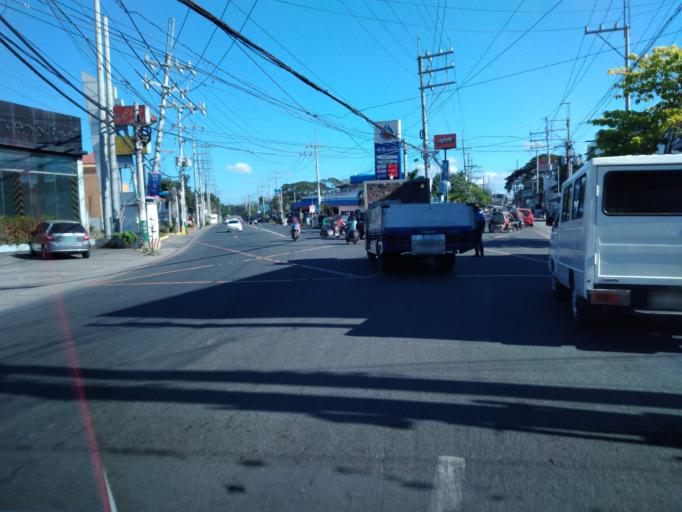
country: PH
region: Central Luzon
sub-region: Province of Bulacan
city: Santa Maria
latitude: 14.8126
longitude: 120.9488
